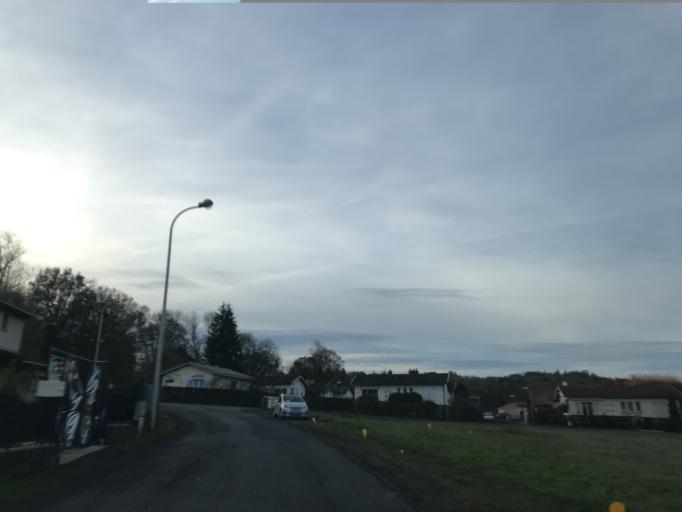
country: FR
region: Auvergne
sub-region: Departement du Puy-de-Dome
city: Courpiere
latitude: 45.7616
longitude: 3.5349
